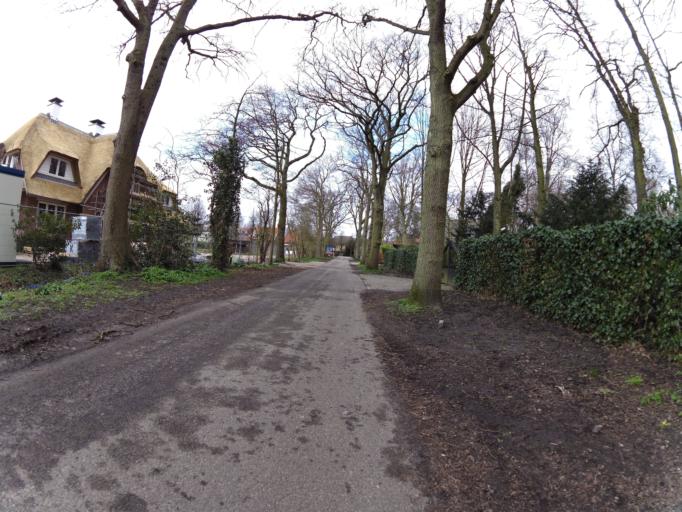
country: NL
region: South Holland
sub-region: Gemeente Brielle
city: Brielle
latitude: 51.9052
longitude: 4.0928
